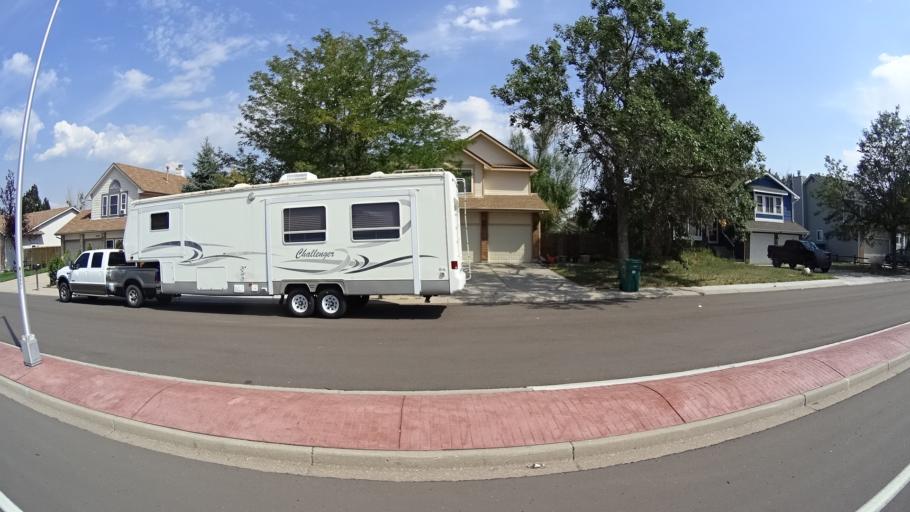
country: US
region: Colorado
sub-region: El Paso County
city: Cimarron Hills
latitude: 38.9259
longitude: -104.7722
